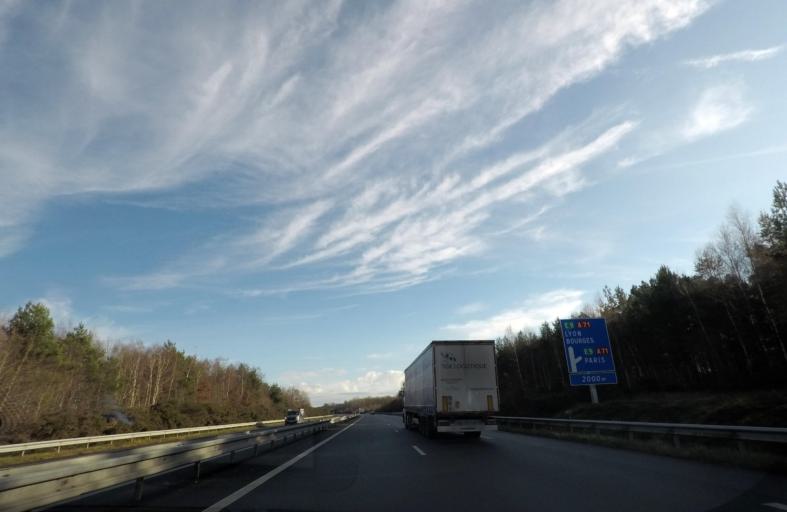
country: FR
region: Centre
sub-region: Departement du Loir-et-Cher
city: Theillay
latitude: 47.2901
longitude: 2.0171
